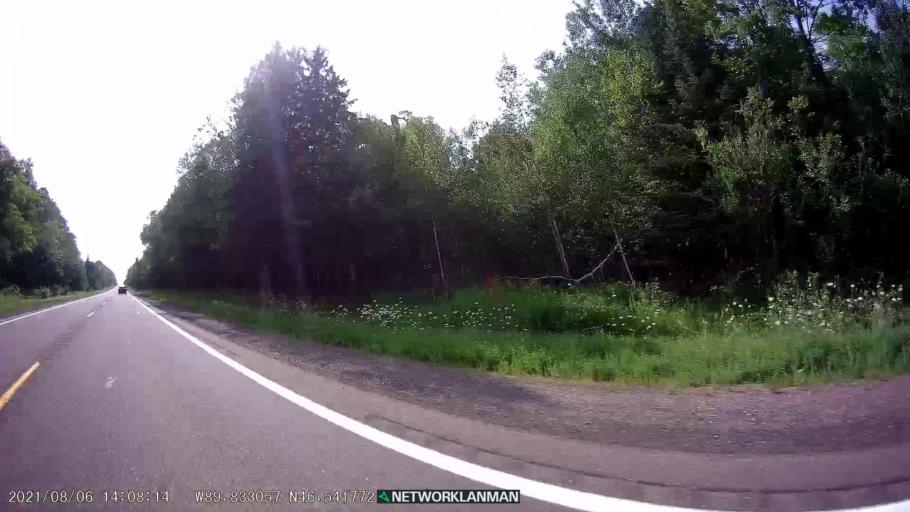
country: US
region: Michigan
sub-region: Gogebic County
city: Wakefield
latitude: 46.5418
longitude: -89.8340
